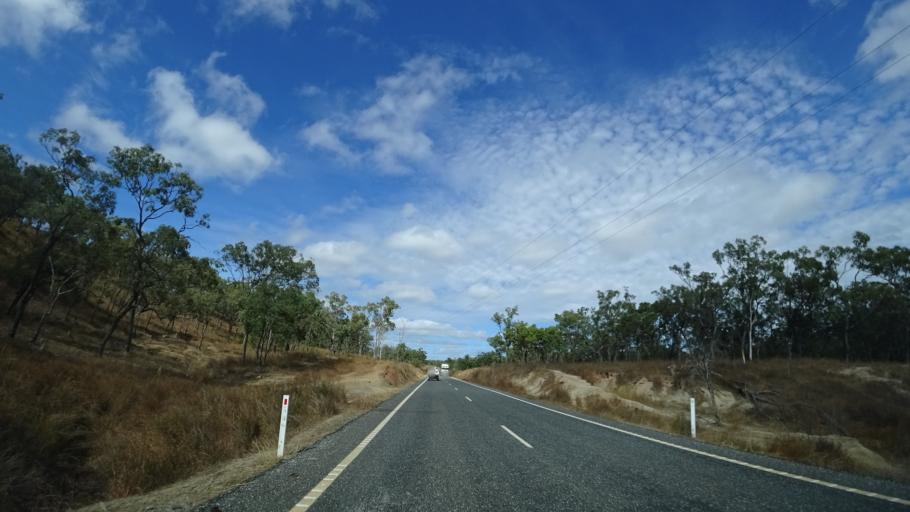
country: AU
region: Queensland
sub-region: Cairns
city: Port Douglas
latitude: -16.2937
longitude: 144.7158
